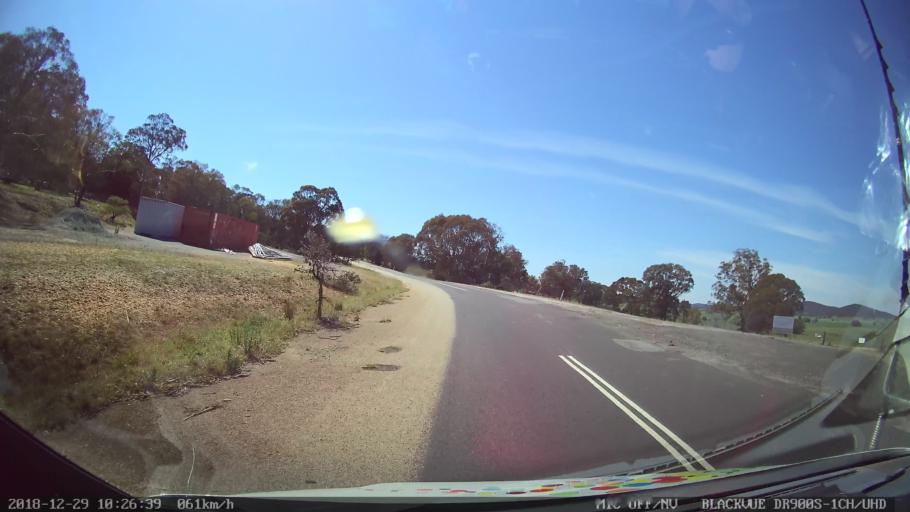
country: AU
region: New South Wales
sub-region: Yass Valley
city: Gundaroo
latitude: -34.9279
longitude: 149.4446
